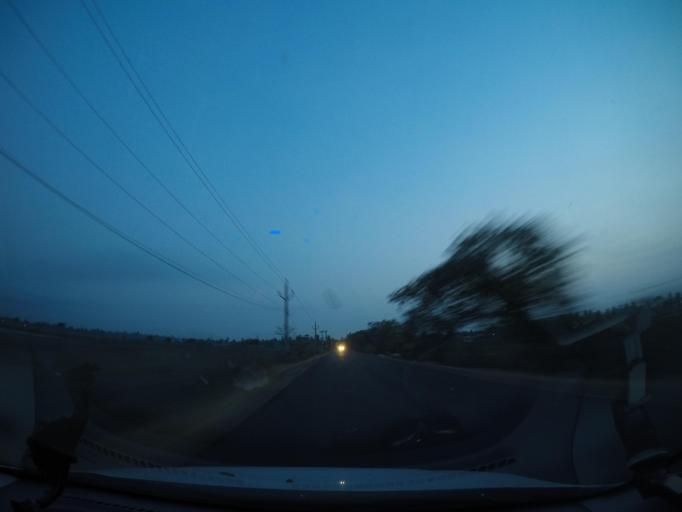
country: IN
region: Andhra Pradesh
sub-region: West Godavari
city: Tadepallegudem
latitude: 16.7771
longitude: 81.4242
